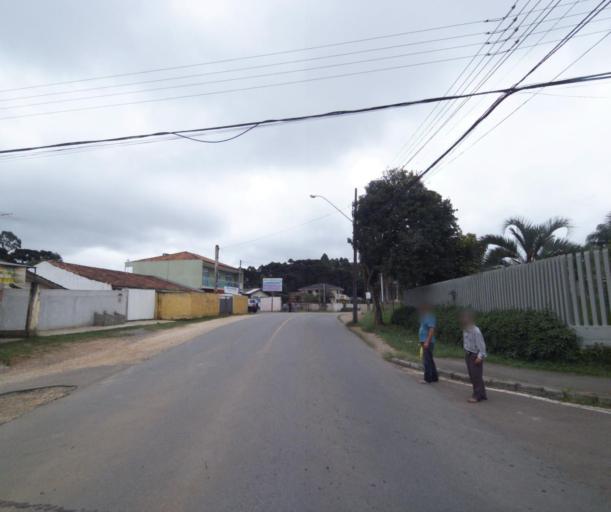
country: BR
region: Parana
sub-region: Quatro Barras
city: Quatro Barras
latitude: -25.3662
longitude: -49.1160
